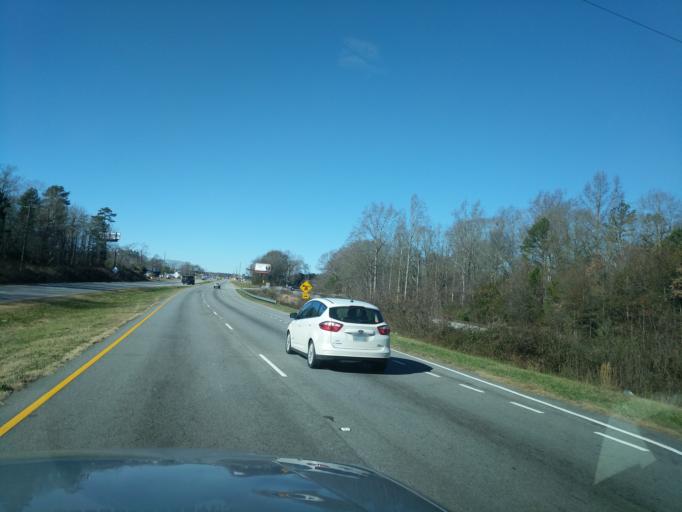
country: US
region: South Carolina
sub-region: Pickens County
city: Clemson
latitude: 34.6914
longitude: -82.8681
